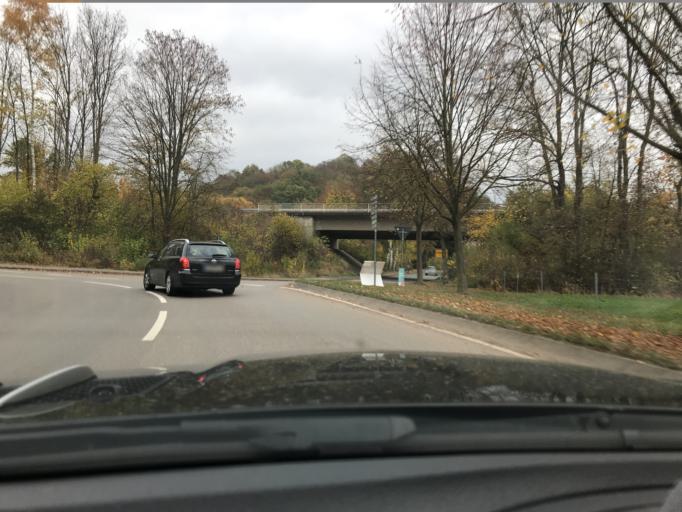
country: DE
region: Hesse
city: Grebenstein
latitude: 51.4413
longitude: 9.4081
